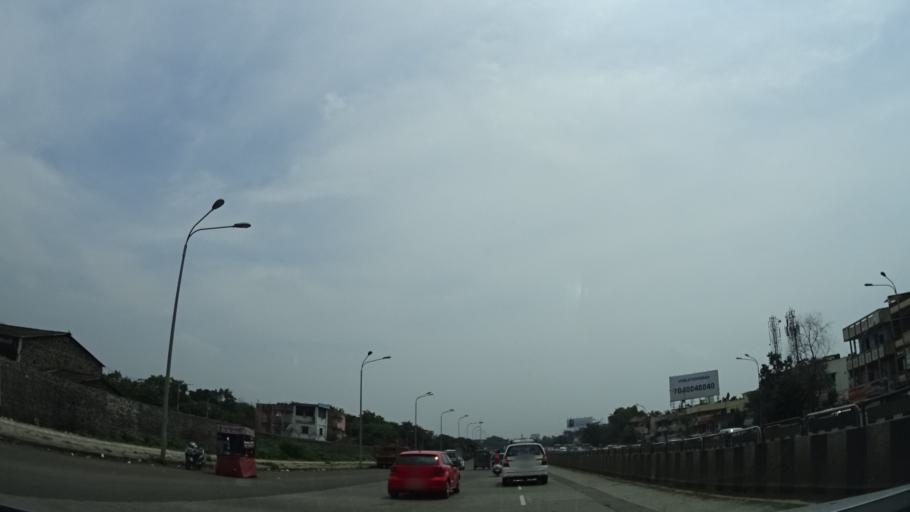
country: IN
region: Maharashtra
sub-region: Pune Division
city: Lohogaon
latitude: 18.5631
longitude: 73.9293
